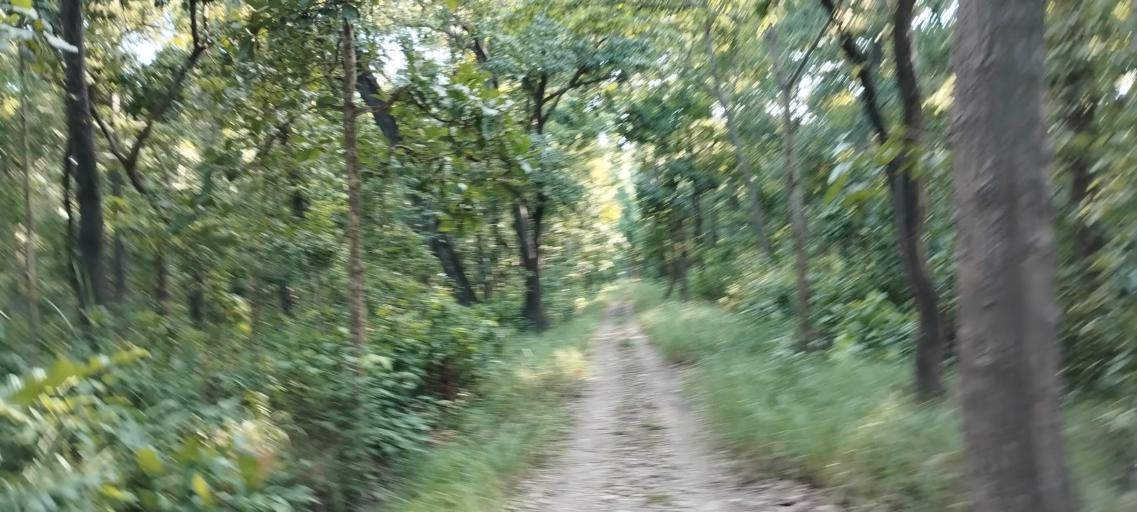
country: NP
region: Far Western
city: Tikapur
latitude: 28.5160
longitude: 81.2734
